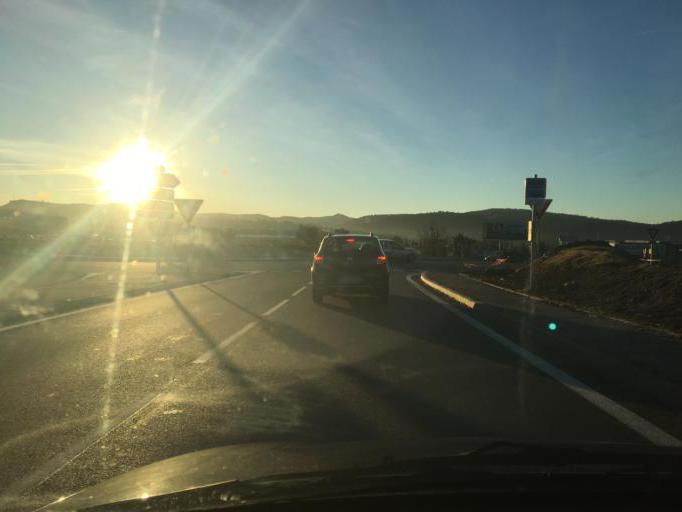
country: FR
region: Provence-Alpes-Cote d'Azur
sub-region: Departement du Var
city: Les Arcs
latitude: 43.4542
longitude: 6.4902
